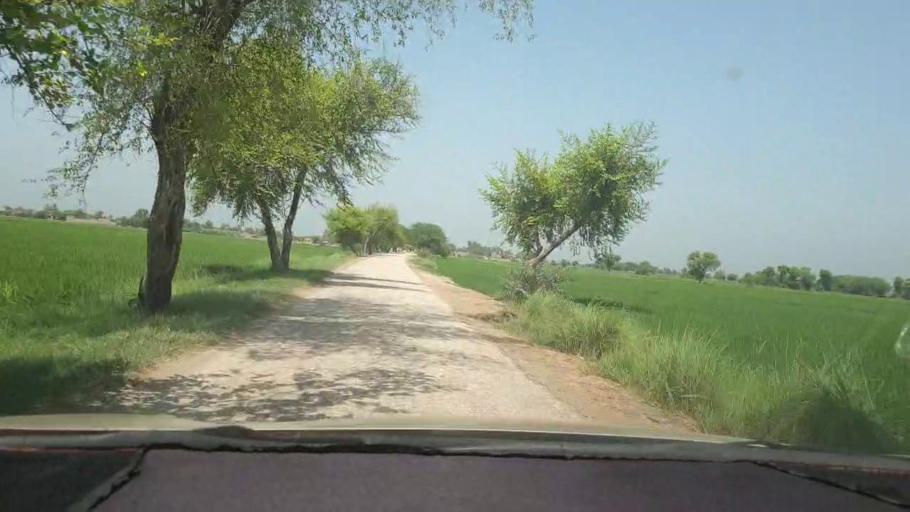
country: PK
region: Sindh
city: Kambar
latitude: 27.6193
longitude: 68.0538
